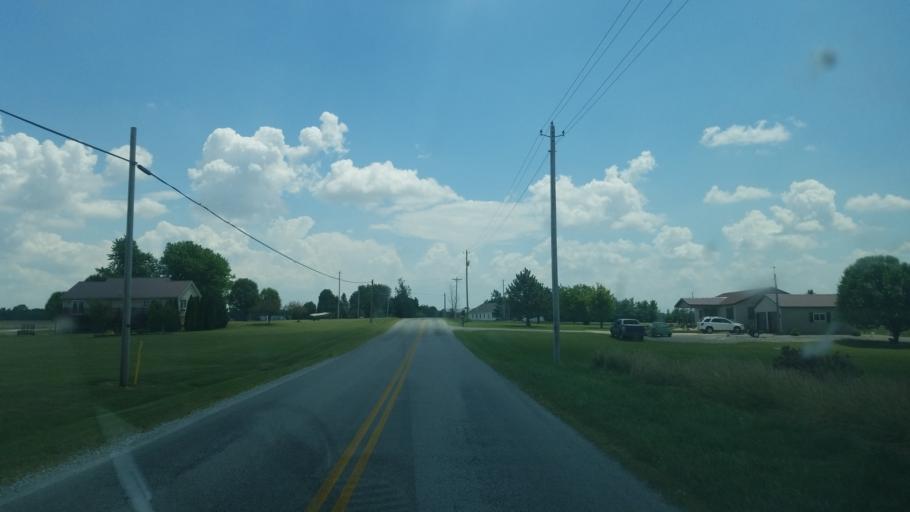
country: US
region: Ohio
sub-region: Hardin County
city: Kenton
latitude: 40.6614
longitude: -83.6568
